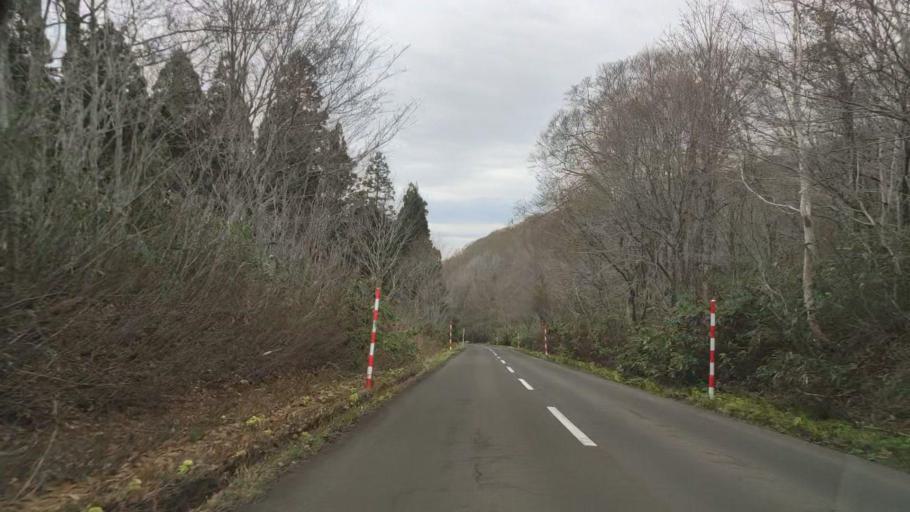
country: JP
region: Akita
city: Hanawa
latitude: 40.4141
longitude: 140.8190
